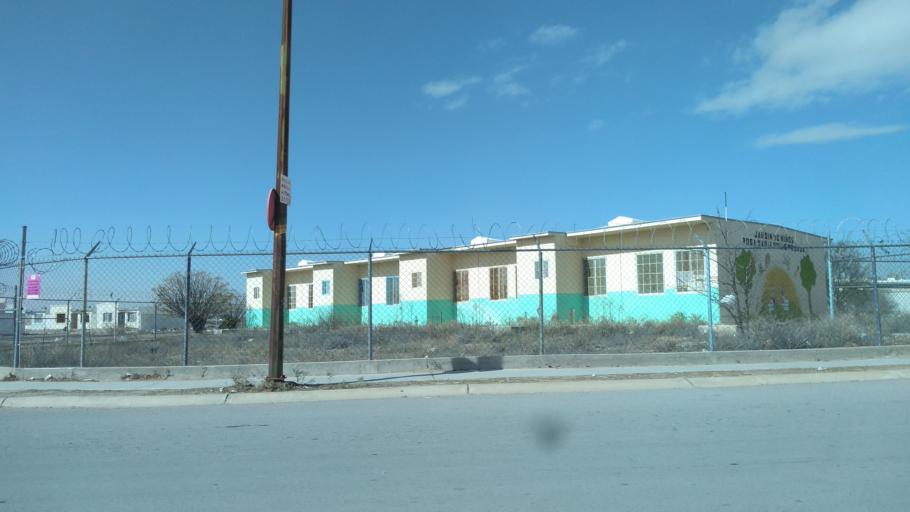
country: US
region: Texas
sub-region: El Paso County
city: San Elizario
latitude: 31.5708
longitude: -106.3303
